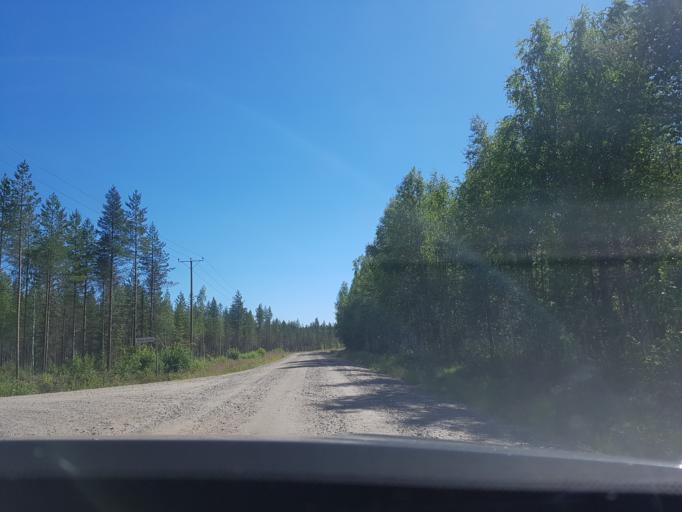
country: FI
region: Kainuu
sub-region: Kehys-Kainuu
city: Kuhmo
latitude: 64.1823
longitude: 29.5931
